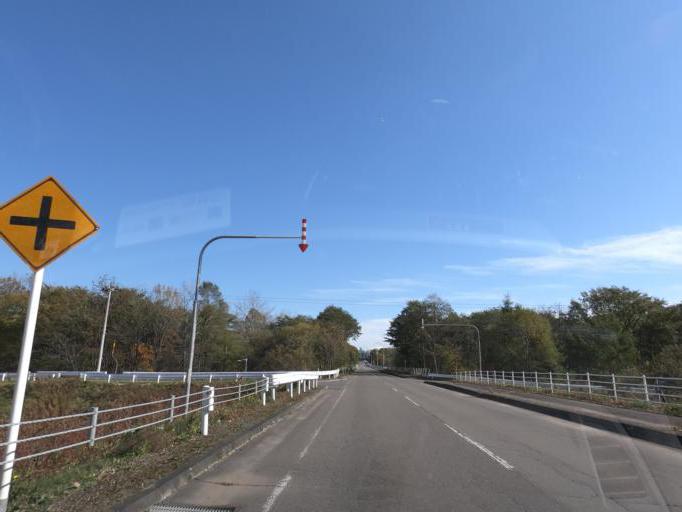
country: JP
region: Hokkaido
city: Otofuke
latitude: 43.2388
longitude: 143.2687
